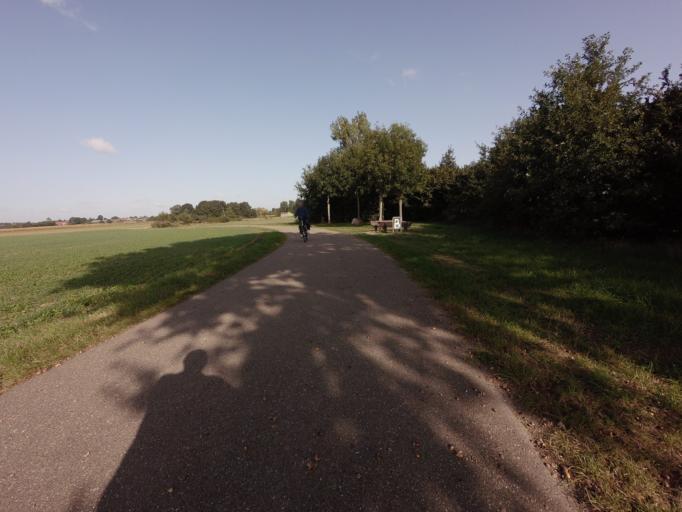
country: NL
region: Limburg
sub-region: Gemeente Roerdalen
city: Melick
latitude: 51.1536
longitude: 6.0332
